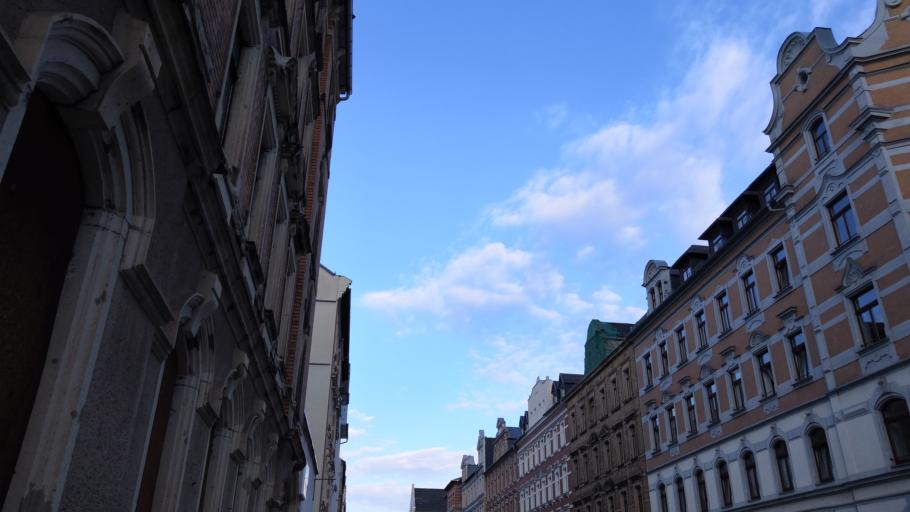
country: DE
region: Saxony
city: Chemnitz
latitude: 50.8418
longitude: 12.9380
